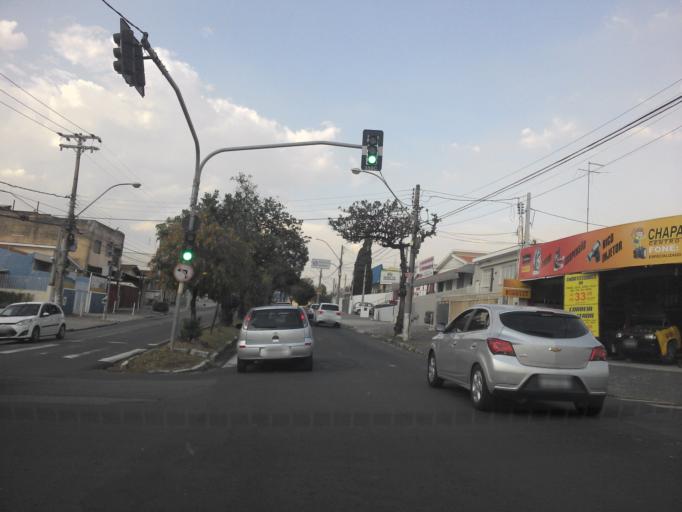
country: BR
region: Sao Paulo
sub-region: Campinas
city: Campinas
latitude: -22.8947
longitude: -47.0952
